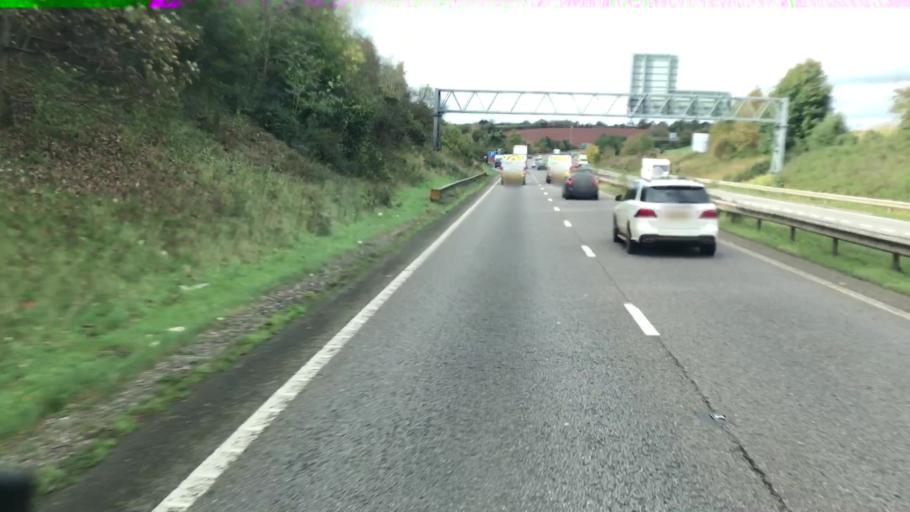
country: GB
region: England
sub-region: Devon
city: Exminster
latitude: 50.6875
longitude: -3.5298
